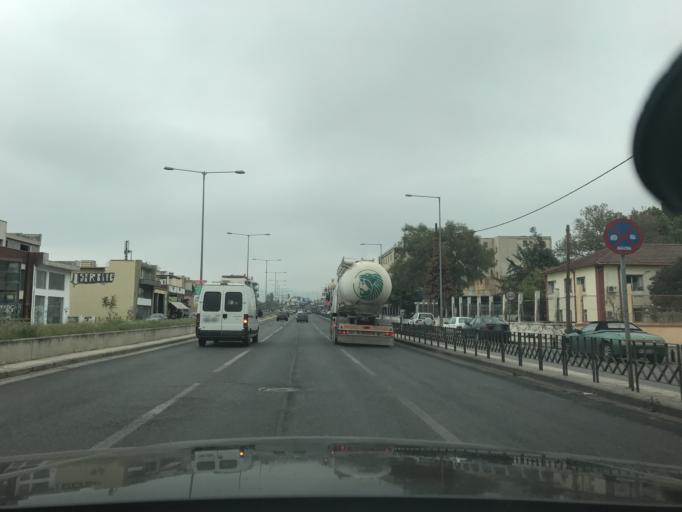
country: GR
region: Central Macedonia
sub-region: Nomos Thessalonikis
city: Stavroupoli
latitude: 40.6688
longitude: 22.9380
